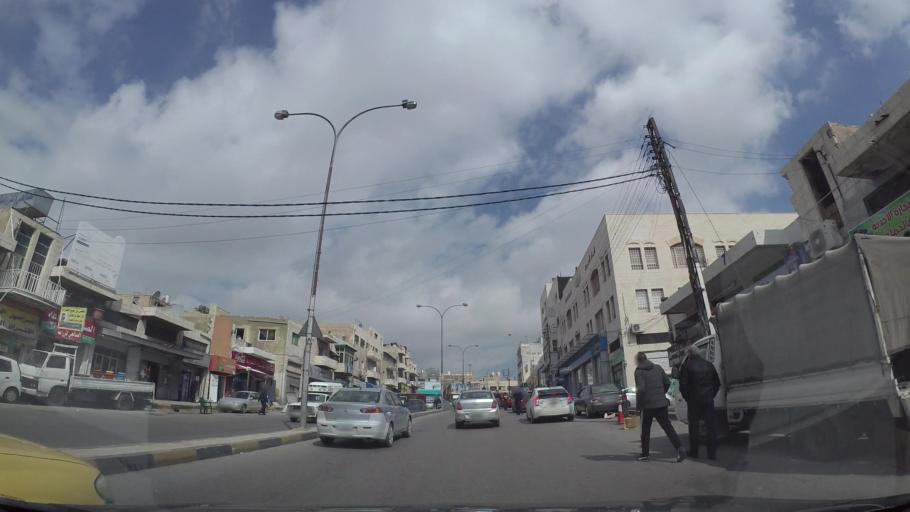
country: JO
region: Amman
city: Al Quwaysimah
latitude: 31.9309
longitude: 35.9338
